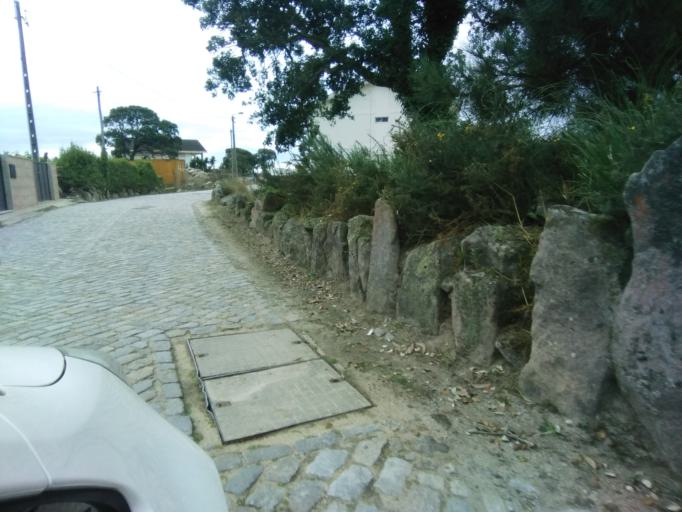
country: PT
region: Porto
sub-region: Matosinhos
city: Santa Cruz do Bispo
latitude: 41.2317
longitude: -8.7096
